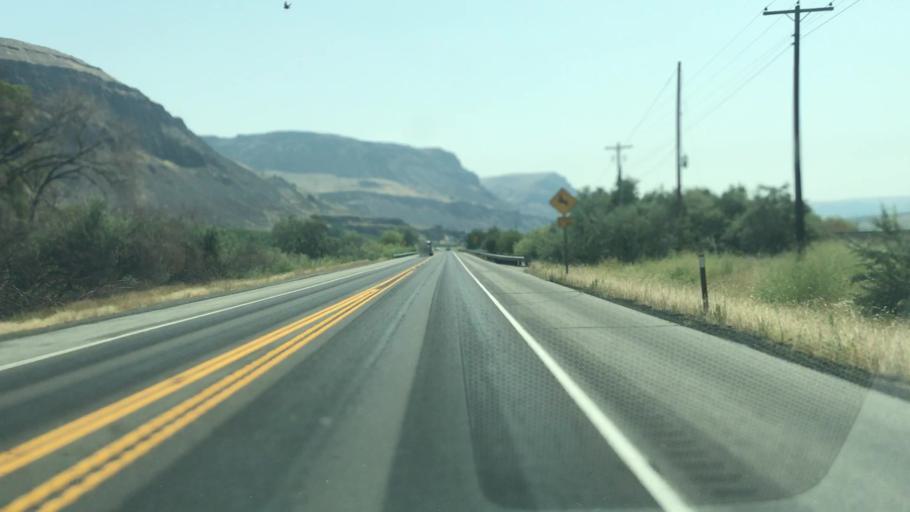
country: US
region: Washington
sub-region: Chelan County
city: South Wenatchee
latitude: 47.3670
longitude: -120.1255
